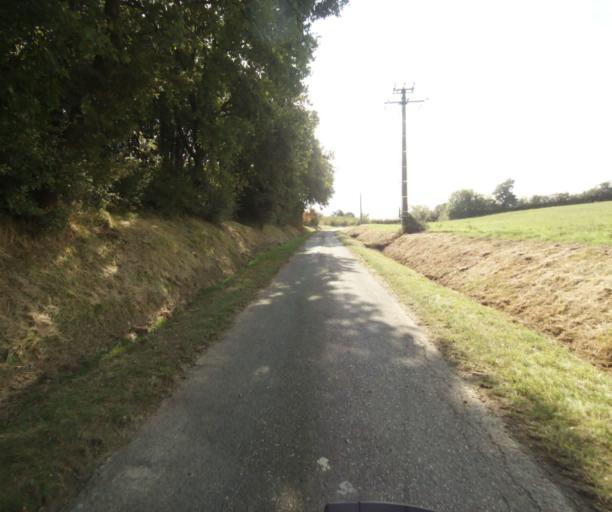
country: FR
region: Midi-Pyrenees
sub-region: Departement du Tarn-et-Garonne
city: Finhan
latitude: 43.8795
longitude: 1.1867
